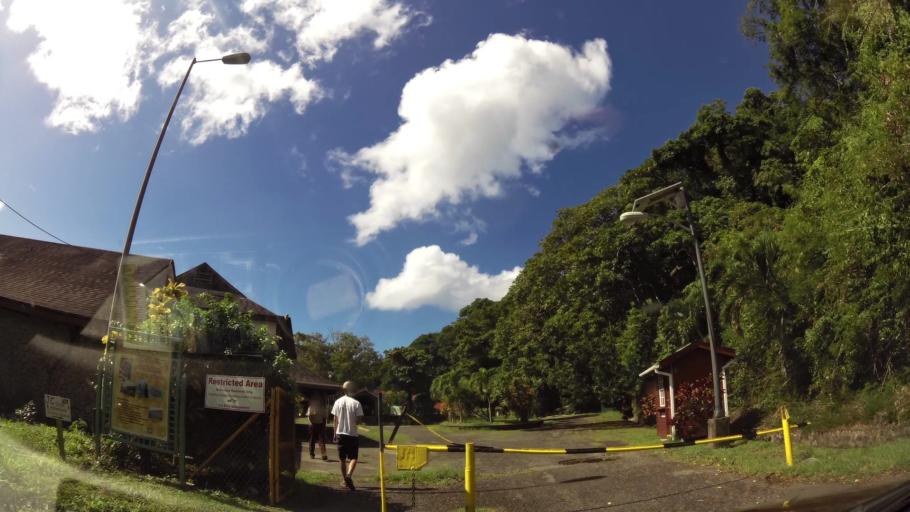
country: DM
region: Saint John
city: Portsmouth
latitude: 15.5830
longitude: -61.4715
